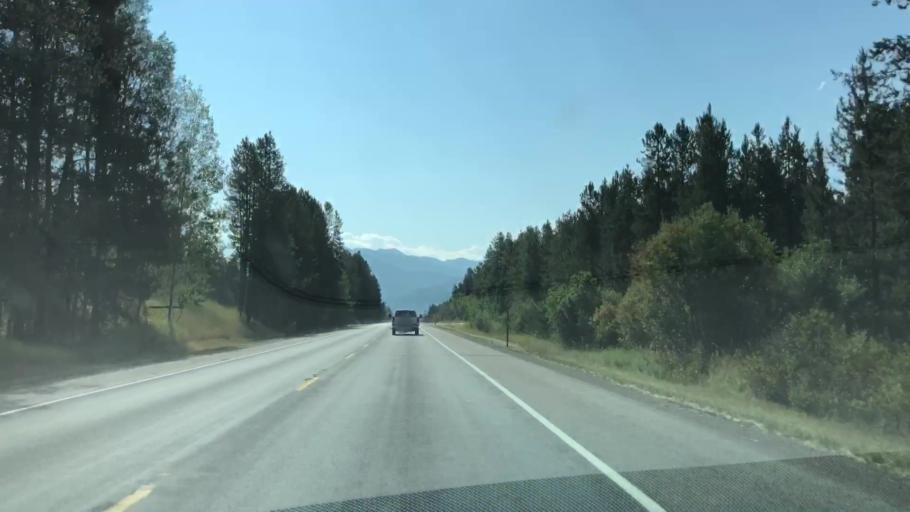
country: US
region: Wyoming
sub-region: Teton County
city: Hoback
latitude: 43.1986
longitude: -111.0422
